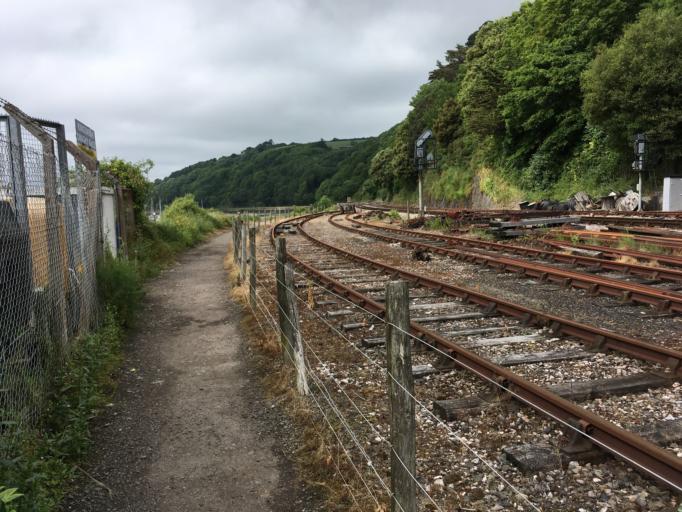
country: GB
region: England
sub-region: Devon
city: Dartmouth
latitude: 50.3522
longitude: -3.5704
